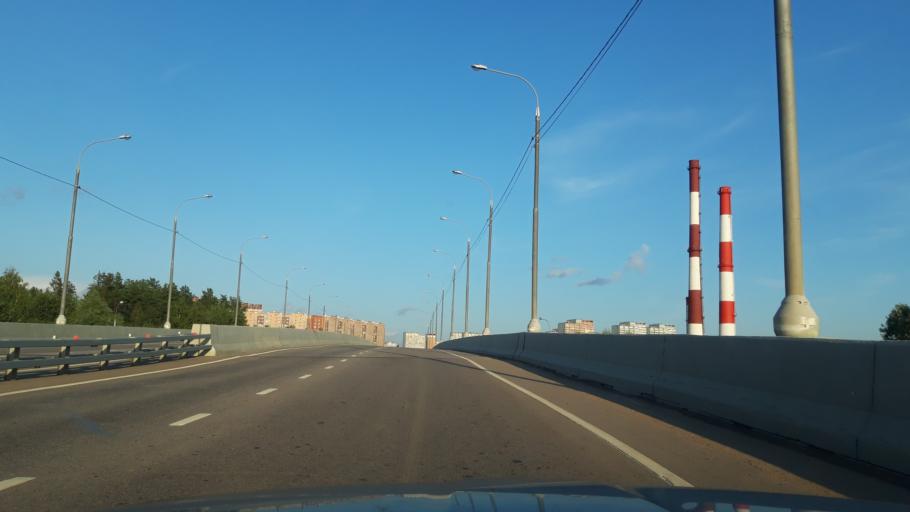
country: RU
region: Moskovskaya
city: Alabushevo
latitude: 55.9953
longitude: 37.1597
